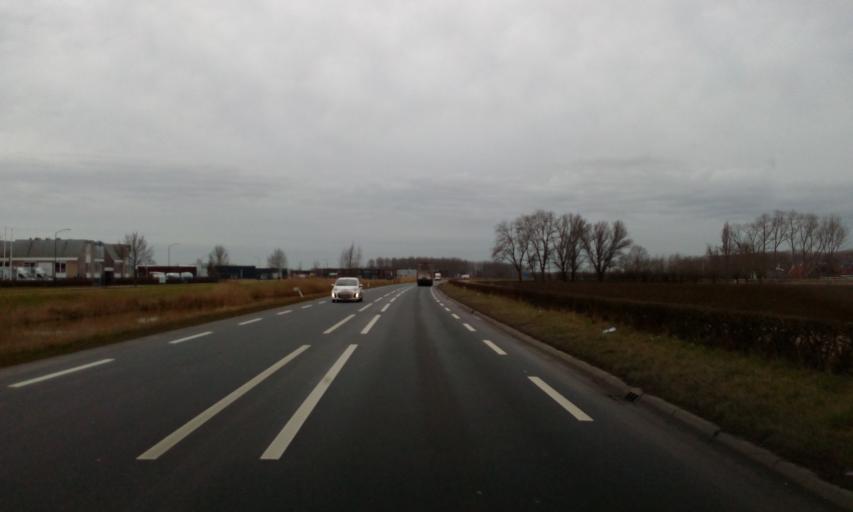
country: NL
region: North Brabant
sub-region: Gemeente Woudrichem
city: Woudrichem
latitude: 51.7840
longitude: 5.0317
